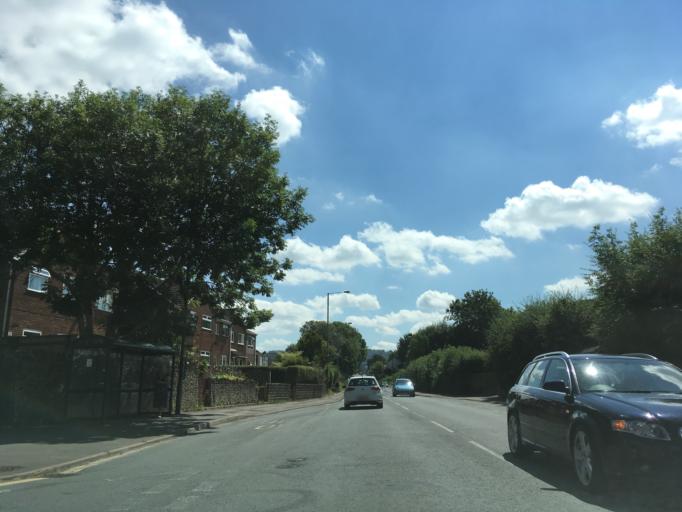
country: GB
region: England
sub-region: Gloucestershire
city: Churchdown
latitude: 51.8458
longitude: -2.1591
